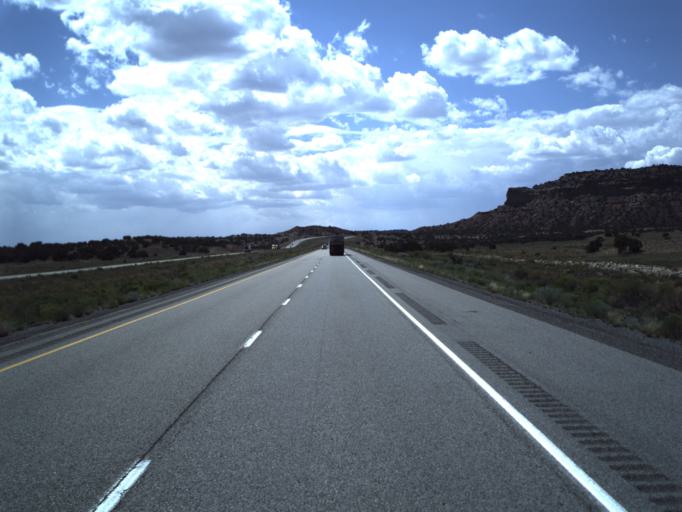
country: US
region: Utah
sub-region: Emery County
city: Castle Dale
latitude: 38.8710
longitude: -110.6912
